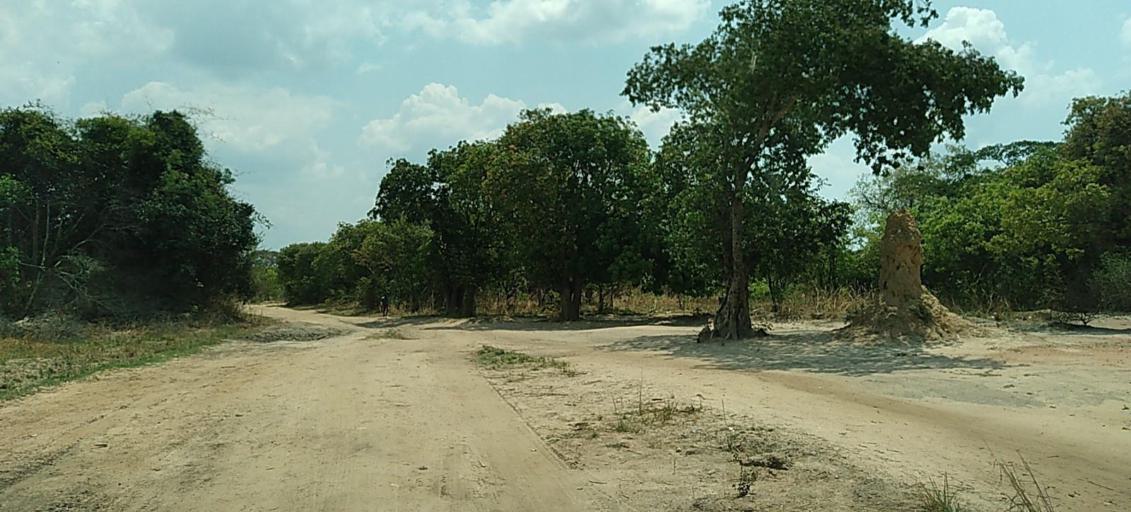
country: ZM
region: Copperbelt
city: Luanshya
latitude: -13.1577
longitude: 28.3106
